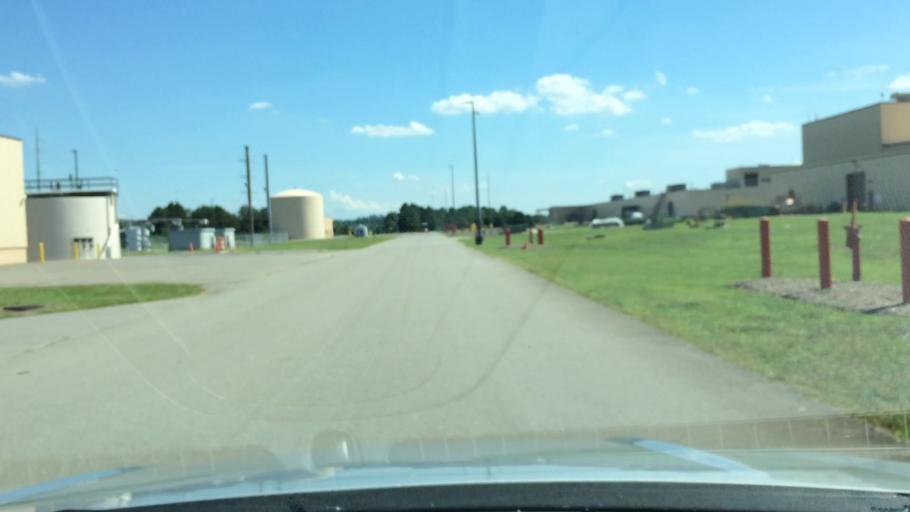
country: US
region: Tennessee
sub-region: McMinn County
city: Athens
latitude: 35.4769
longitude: -84.6425
